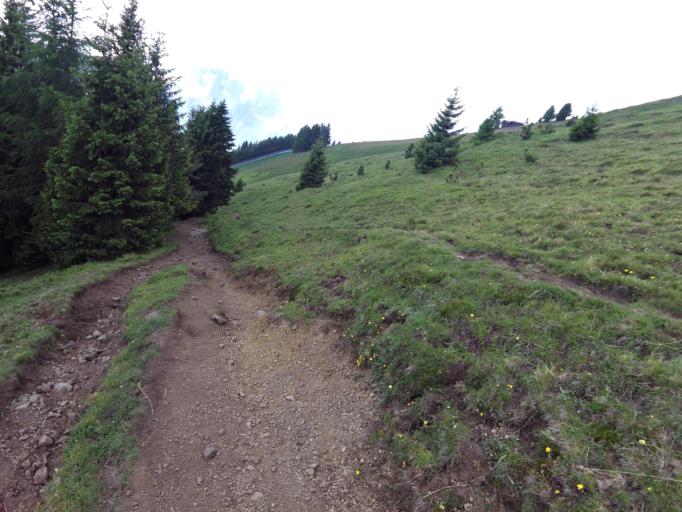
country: IT
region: Trentino-Alto Adige
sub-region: Bolzano
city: Siusi
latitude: 46.5475
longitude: 11.6135
